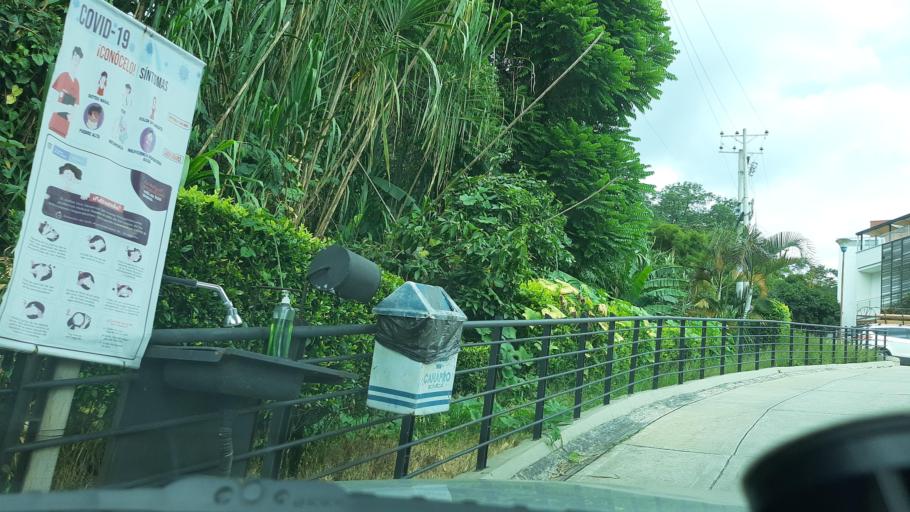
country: CO
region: Boyaca
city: Moniquira
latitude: 5.8814
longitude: -73.5774
